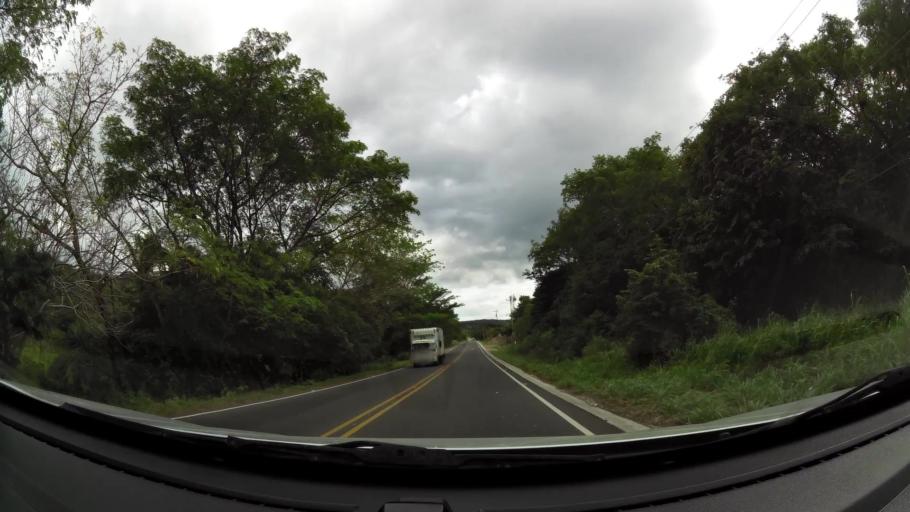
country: CR
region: Guanacaste
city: Nandayure
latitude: 10.2487
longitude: -85.2272
